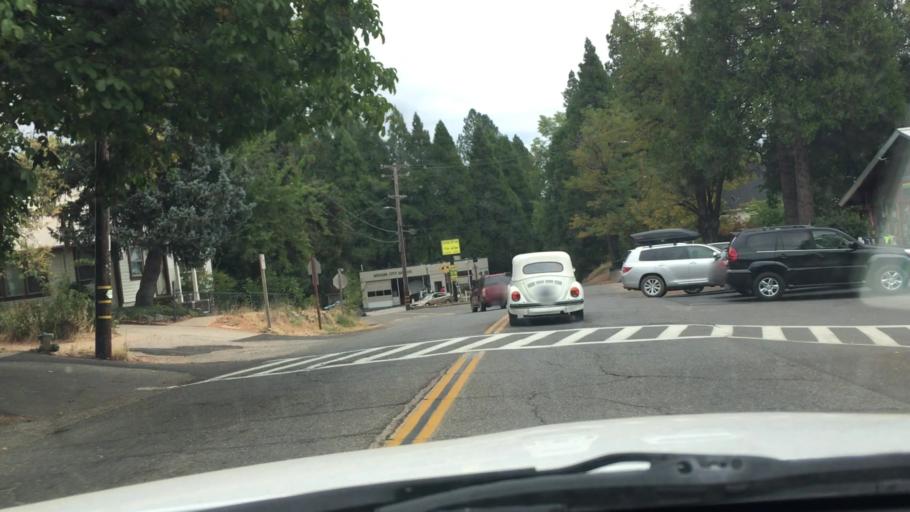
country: US
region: California
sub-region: Nevada County
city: Nevada City
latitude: 39.2574
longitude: -121.0222
